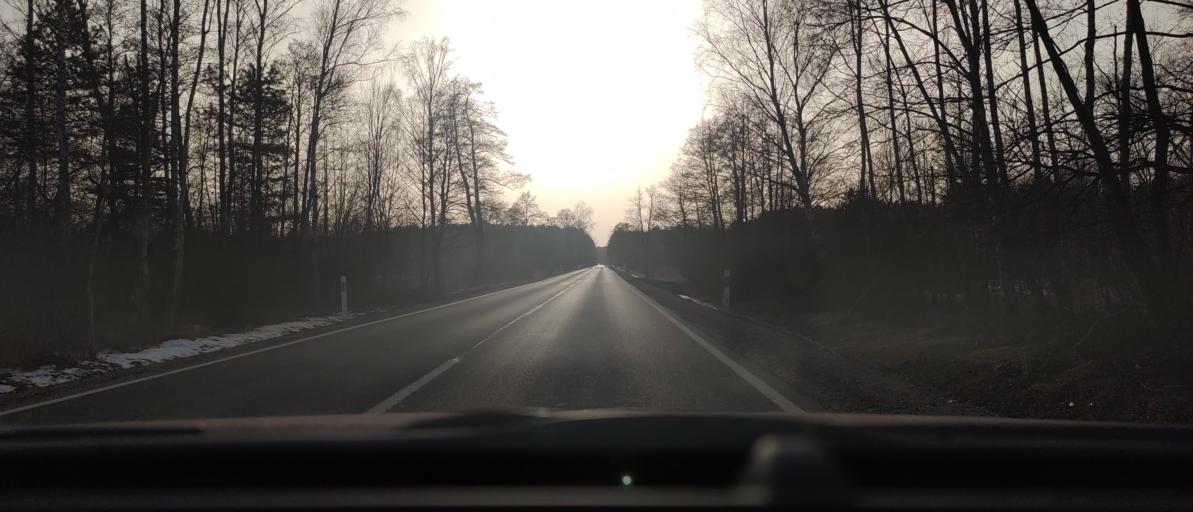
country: PL
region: Masovian Voivodeship
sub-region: Powiat bialobrzeski
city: Sucha
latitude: 51.6344
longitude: 20.8990
